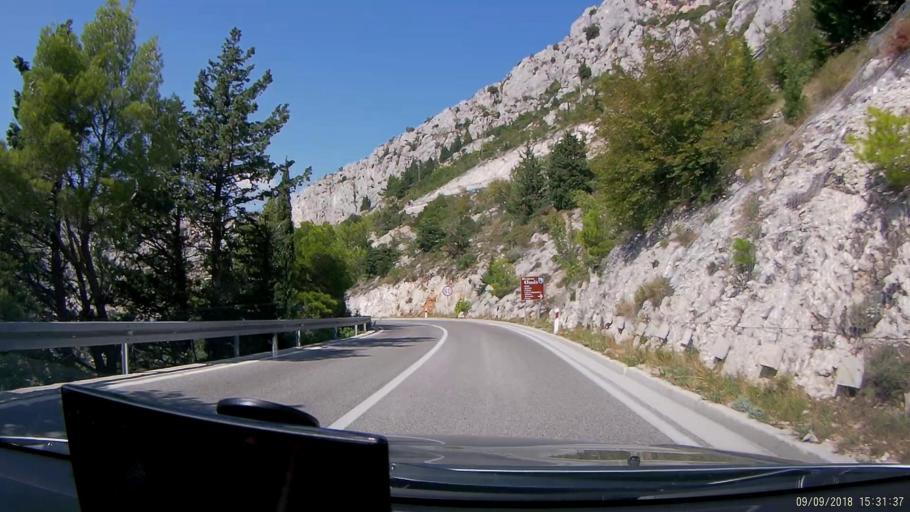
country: HR
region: Splitsko-Dalmatinska
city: Donja Brela
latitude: 43.3991
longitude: 16.8942
